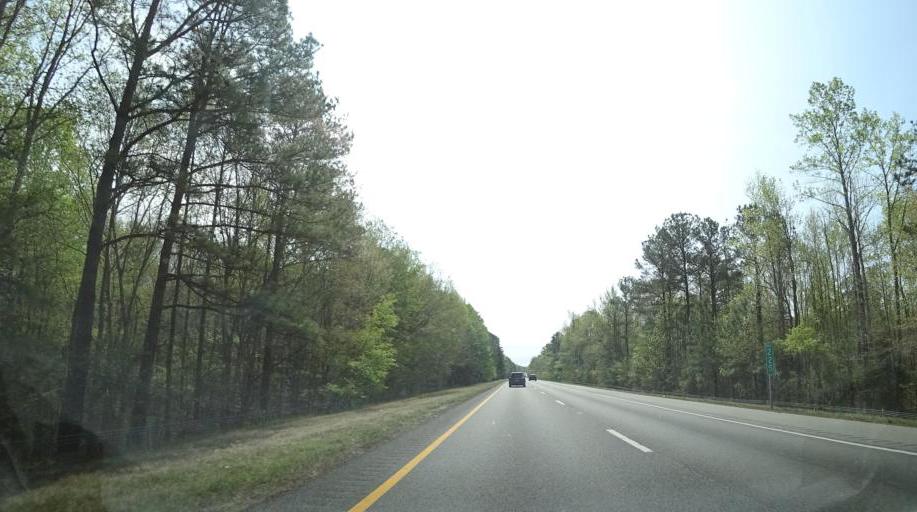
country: US
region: Virginia
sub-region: King William County
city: West Point
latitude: 37.4397
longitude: -76.8536
